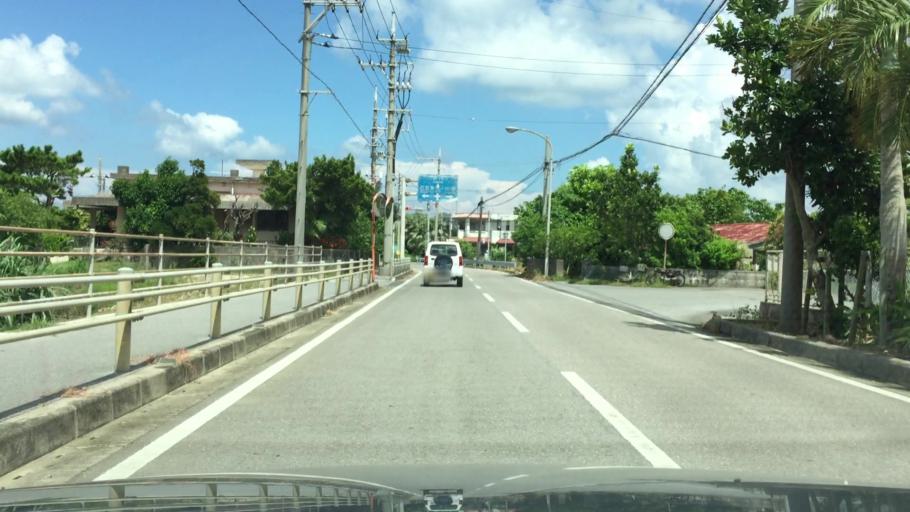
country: JP
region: Okinawa
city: Ishigaki
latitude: 24.3947
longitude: 124.1574
